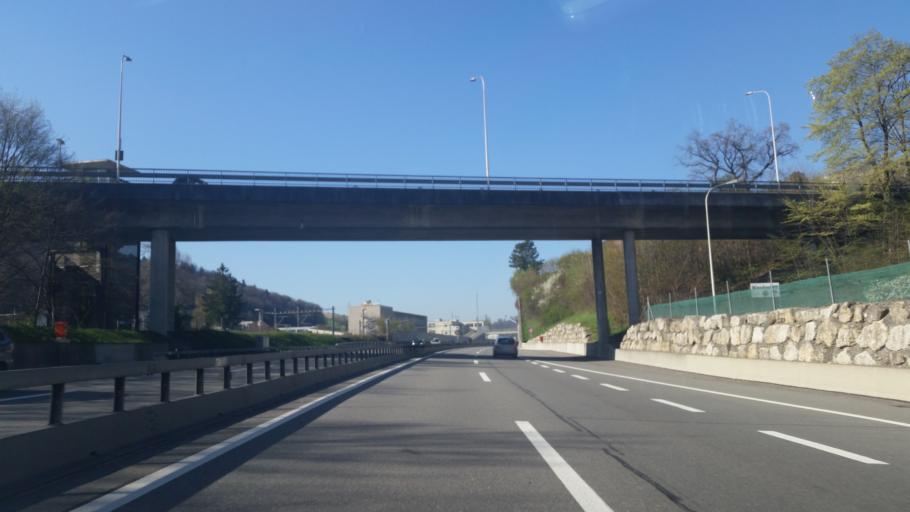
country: CH
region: Fribourg
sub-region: Sense District
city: Flamatt
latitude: 46.8883
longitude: 7.3260
